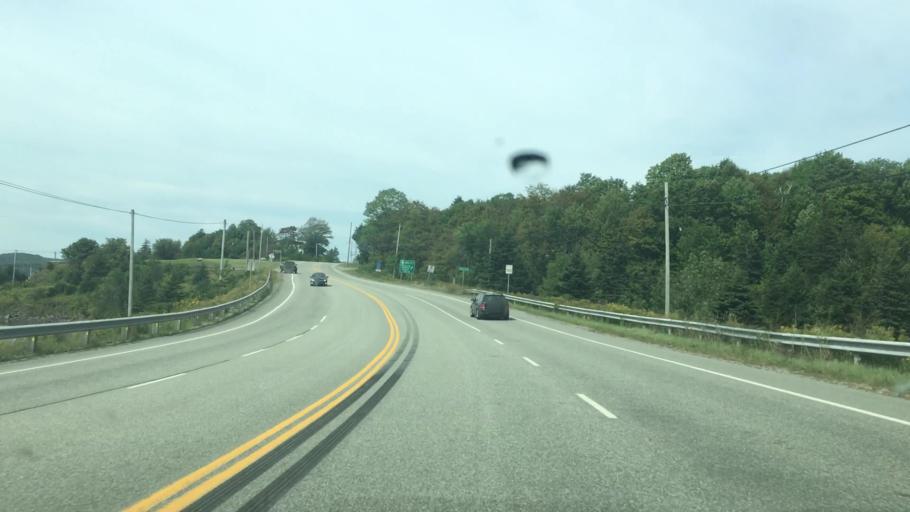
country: CA
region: Nova Scotia
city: Port Hawkesbury
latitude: 45.6444
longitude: -61.3968
